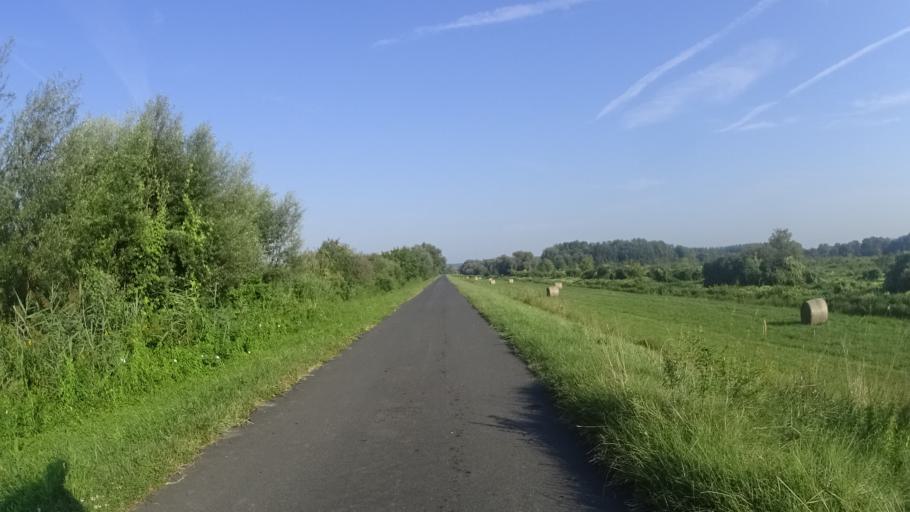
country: HU
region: Zala
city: Sarmellek
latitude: 46.6535
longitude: 17.1434
